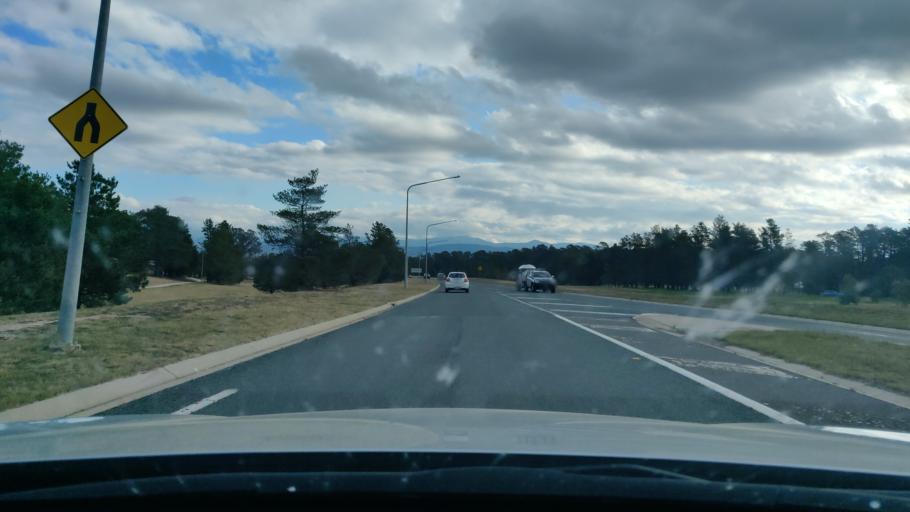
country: AU
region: Australian Capital Territory
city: Macarthur
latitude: -35.4126
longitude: 149.1244
